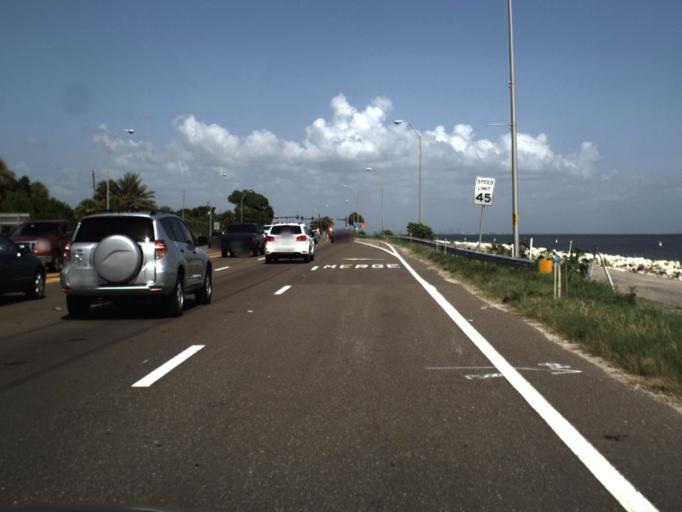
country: US
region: Florida
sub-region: Pinellas County
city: Safety Harbor
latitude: 27.9606
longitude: -82.7032
